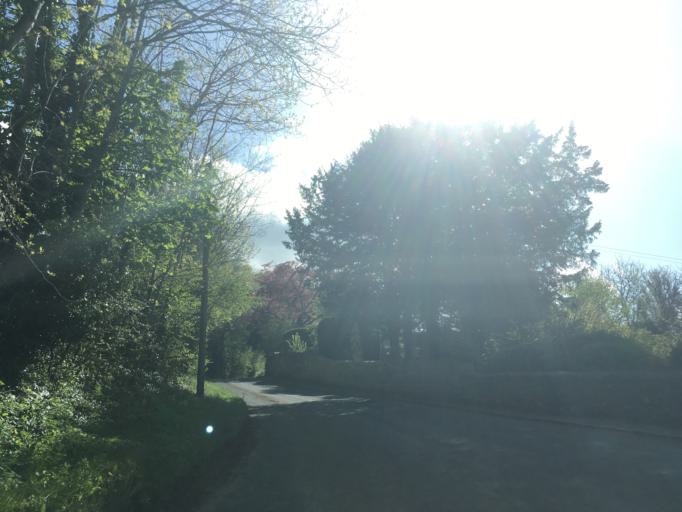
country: GB
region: England
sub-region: Gloucestershire
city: Stonehouse
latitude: 51.7337
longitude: -2.2447
